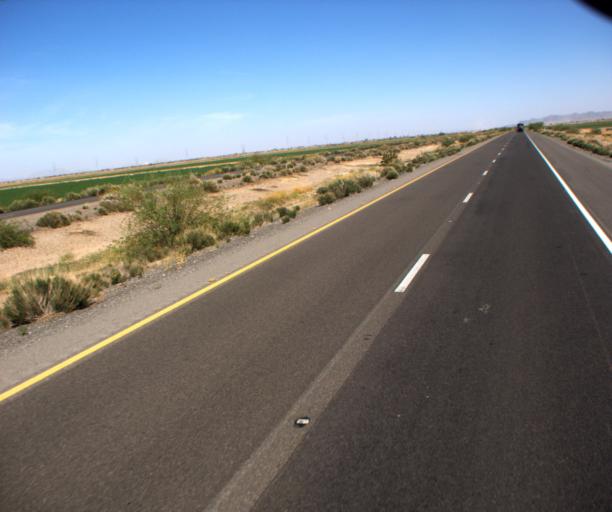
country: US
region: Arizona
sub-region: Pinal County
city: Casa Grande
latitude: 32.8280
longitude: -111.9065
